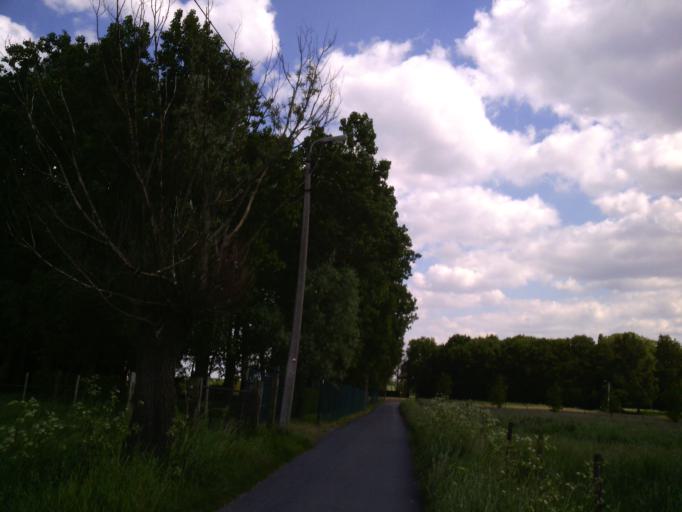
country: BE
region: Flanders
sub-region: Provincie West-Vlaanderen
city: Wevelgem
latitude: 50.7869
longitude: 3.1805
